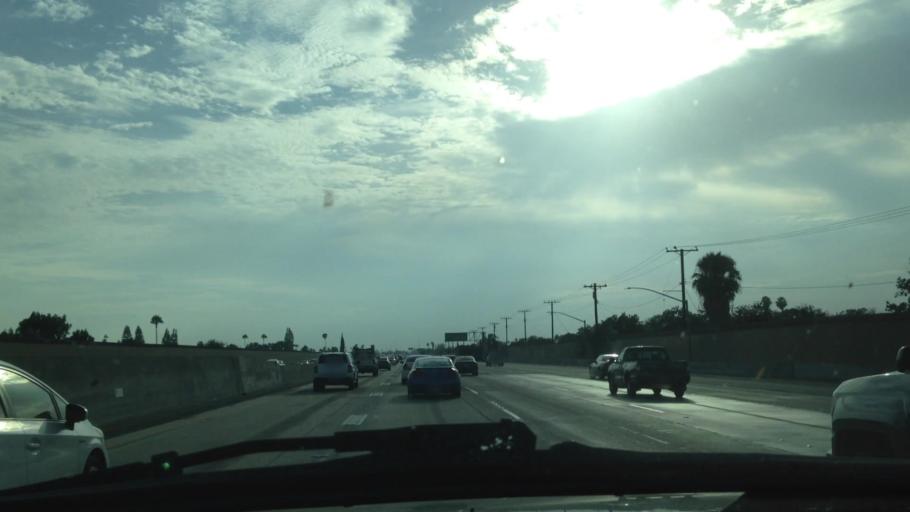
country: US
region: California
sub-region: Orange County
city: Fullerton
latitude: 33.8544
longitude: -117.9459
